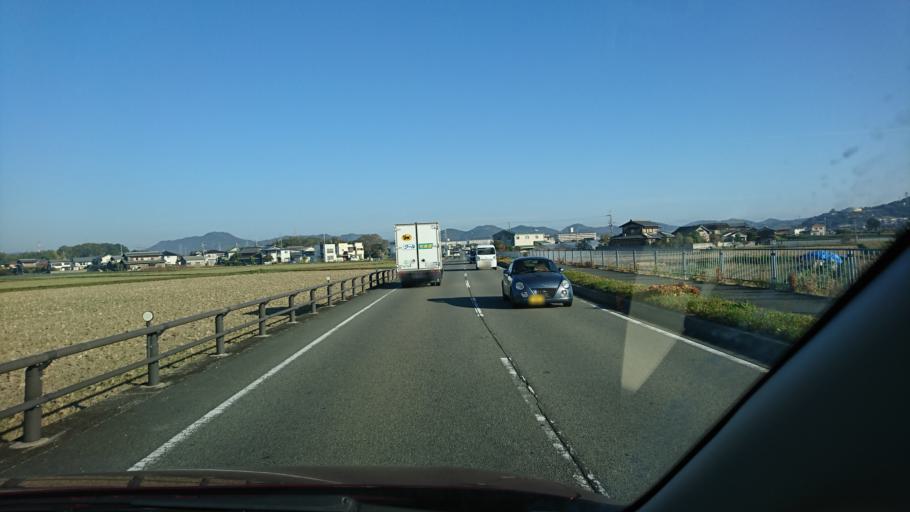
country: JP
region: Hyogo
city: Kakogawacho-honmachi
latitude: 34.7783
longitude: 134.8723
